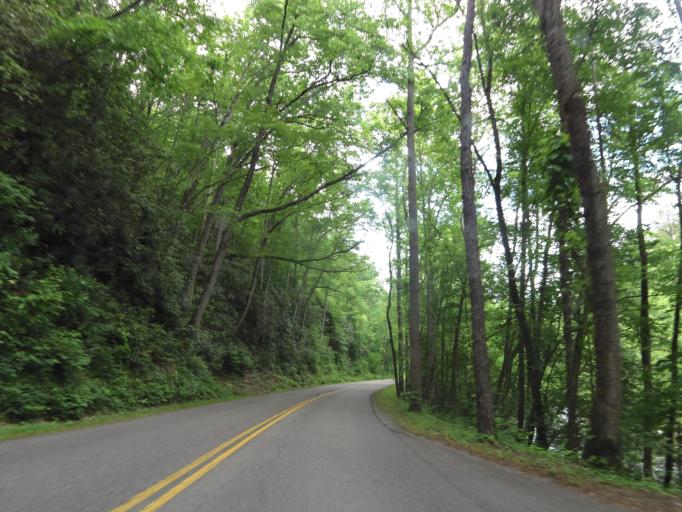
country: US
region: Tennessee
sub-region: Sevier County
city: Gatlinburg
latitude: 35.6733
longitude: -83.6456
